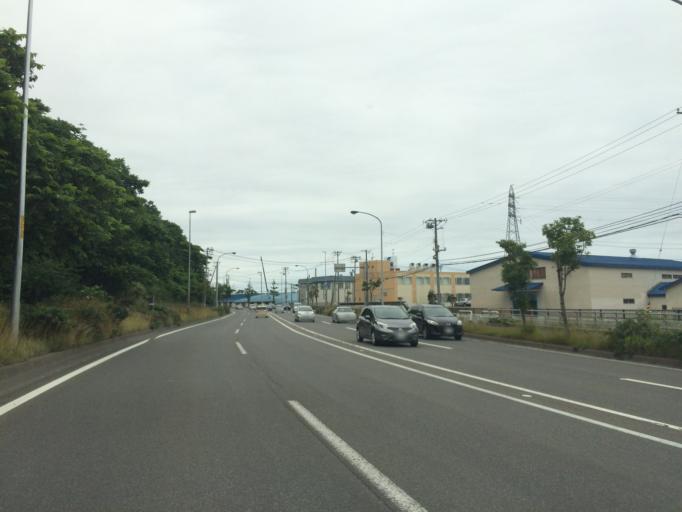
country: JP
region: Hokkaido
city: Otaru
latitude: 43.1367
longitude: 141.1702
